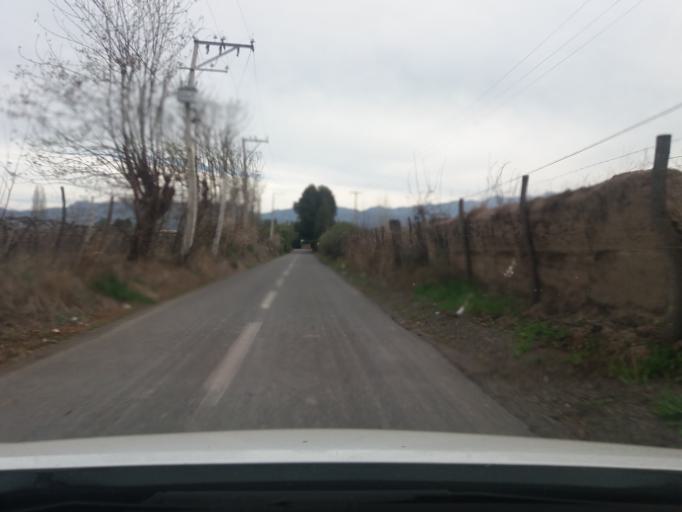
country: CL
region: Valparaiso
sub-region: Provincia de Los Andes
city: Los Andes
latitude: -32.8488
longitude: -70.6290
